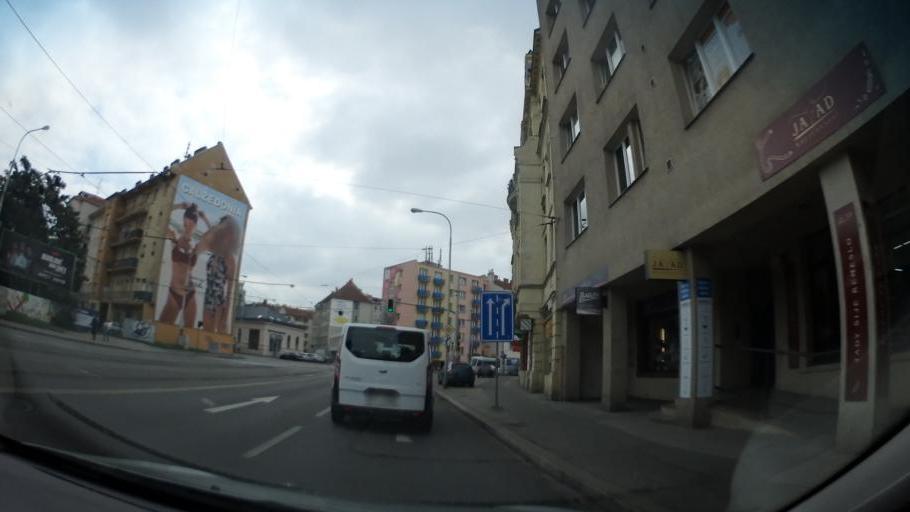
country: CZ
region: South Moravian
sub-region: Mesto Brno
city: Brno
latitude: 49.1895
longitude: 16.5943
